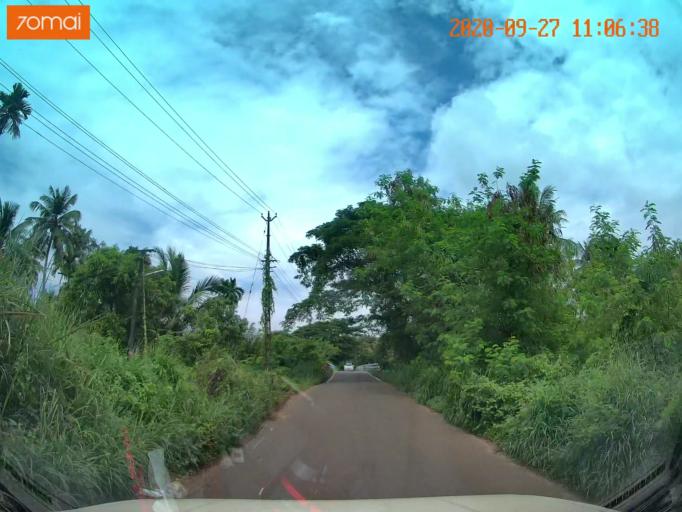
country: IN
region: Kerala
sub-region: Thrissur District
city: Irinjalakuda
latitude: 10.4264
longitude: 76.2406
